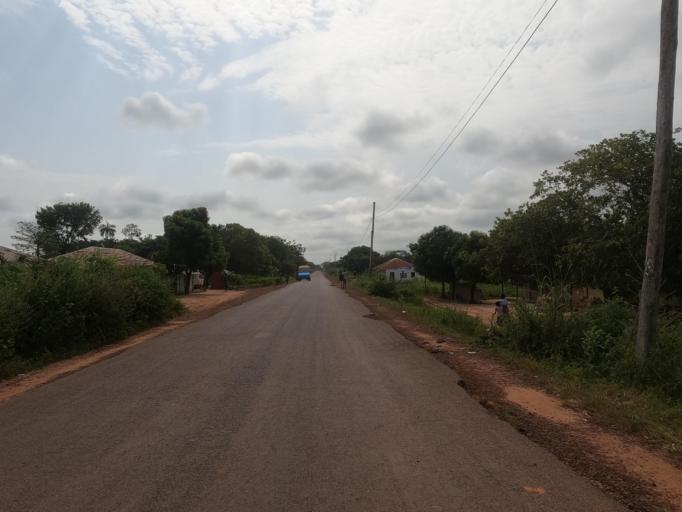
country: SN
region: Ziguinchor
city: Adeane
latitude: 12.3999
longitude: -15.7907
